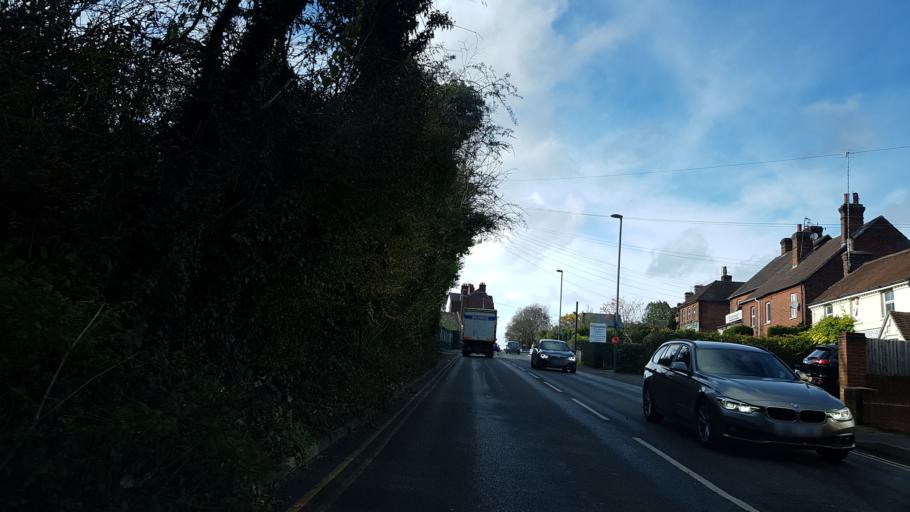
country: GB
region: England
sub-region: Surrey
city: Haslemere
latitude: 51.0882
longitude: -0.7227
